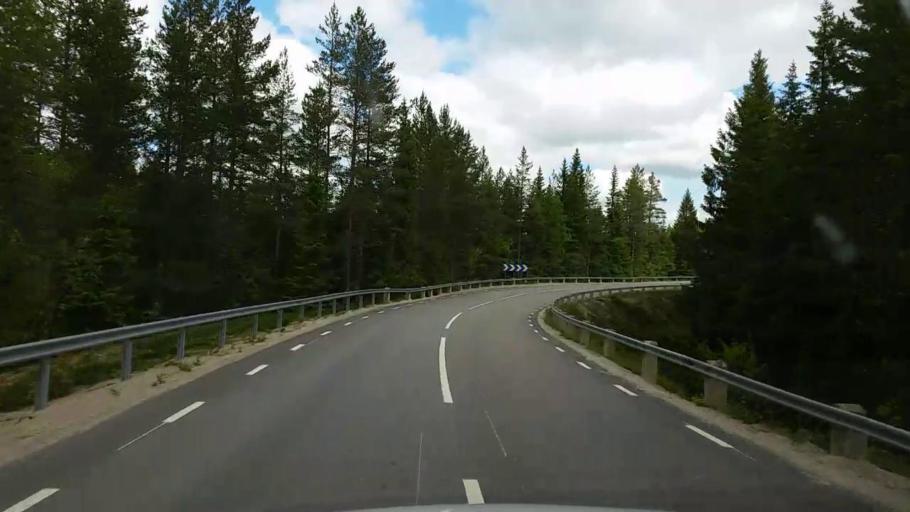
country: SE
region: Gaevleborg
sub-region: Bollnas Kommun
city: Vittsjo
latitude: 61.1196
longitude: 16.1575
